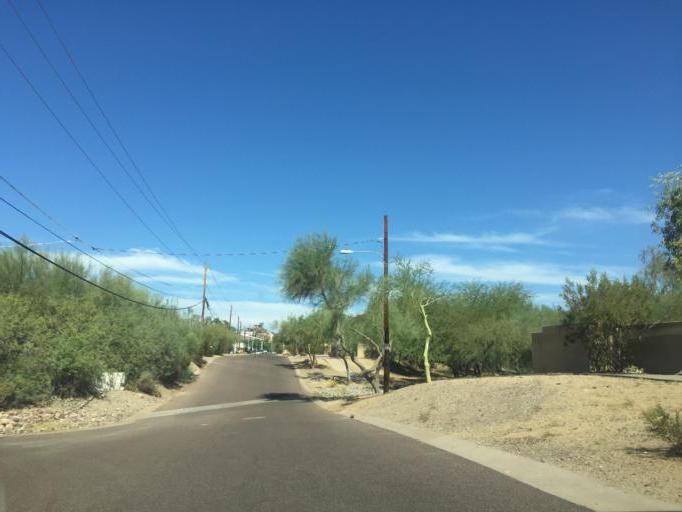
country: US
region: Arizona
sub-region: Maricopa County
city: Phoenix
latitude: 33.5510
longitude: -112.0522
